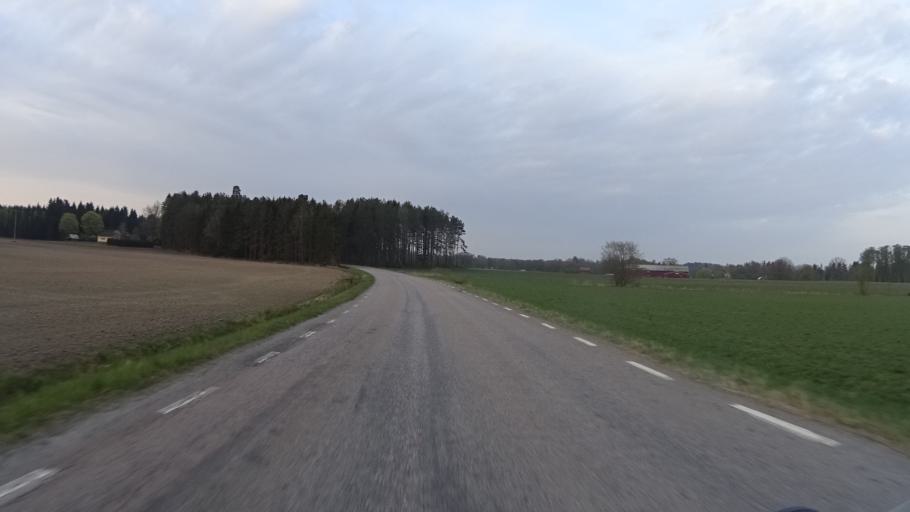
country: SE
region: Vaestra Goetaland
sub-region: Lidkopings Kommun
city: Vinninga
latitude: 58.4397
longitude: 13.3377
